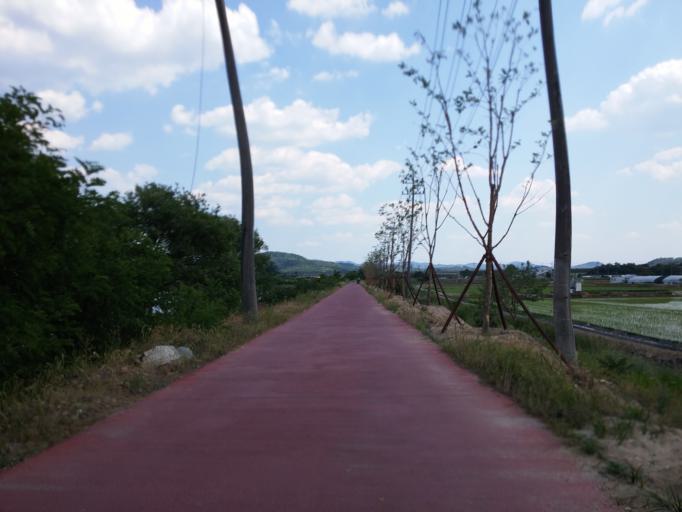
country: KR
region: Chungcheongbuk-do
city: Cheongju-si
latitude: 36.5886
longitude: 127.4988
